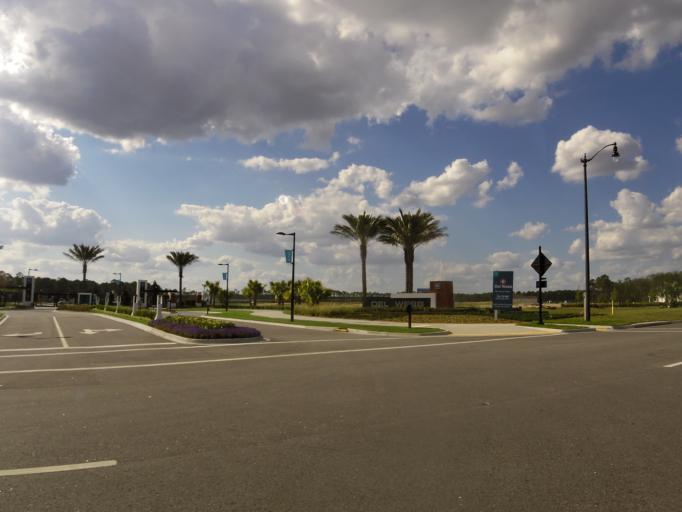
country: US
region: Florida
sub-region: Saint Johns County
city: Palm Valley
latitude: 30.1740
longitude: -81.5065
